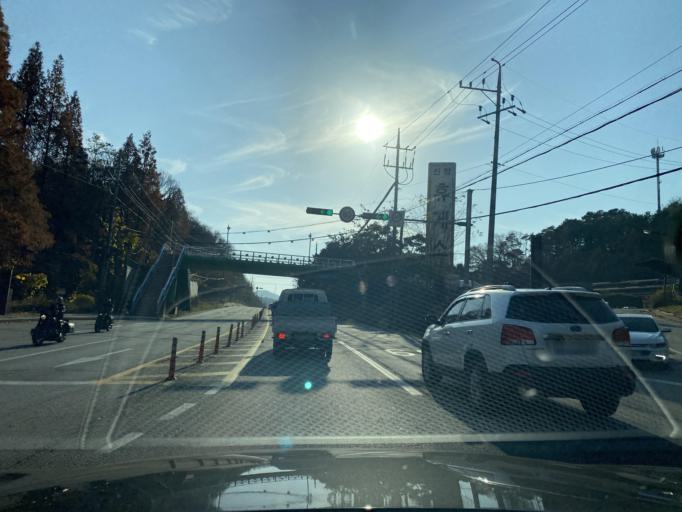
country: KR
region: Chungcheongnam-do
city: Asan
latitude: 36.7695
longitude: 126.9273
